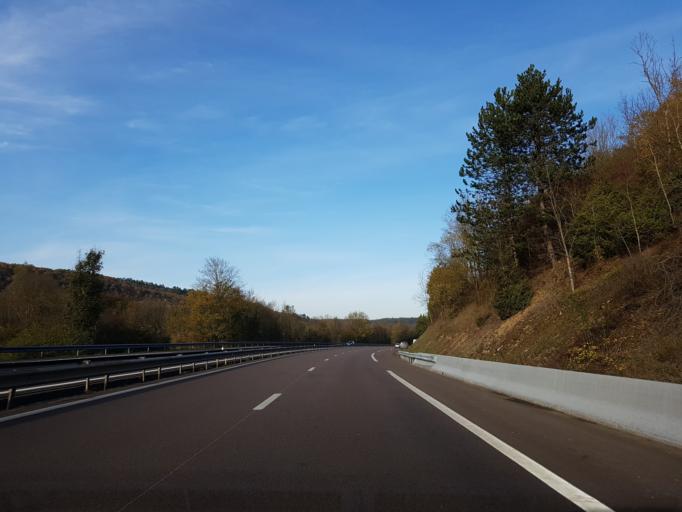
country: FR
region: Bourgogne
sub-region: Departement de la Cote-d'Or
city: Velars-sur-Ouche
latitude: 47.3243
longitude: 4.9338
